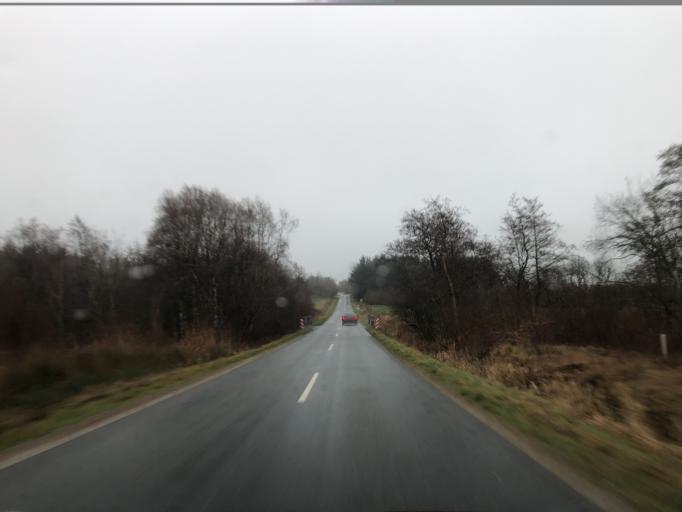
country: DK
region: Central Jutland
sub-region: Holstebro Kommune
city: Ulfborg
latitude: 56.2026
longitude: 8.4100
